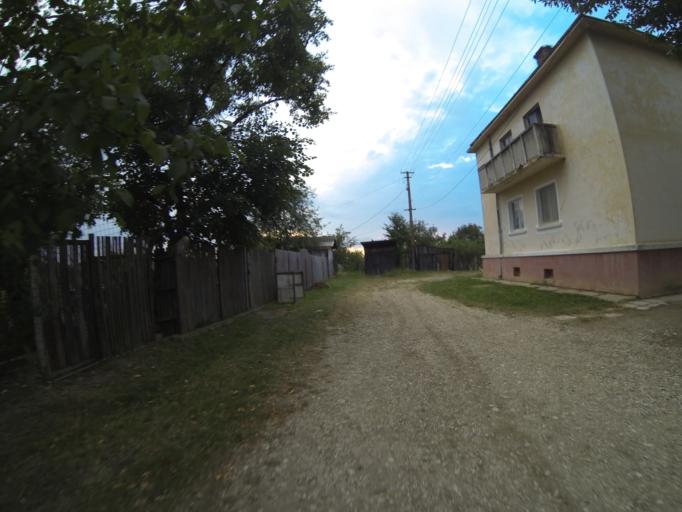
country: RO
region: Brasov
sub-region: Comuna Sinca Veche
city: Sinca Veche
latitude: 45.7677
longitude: 25.1712
